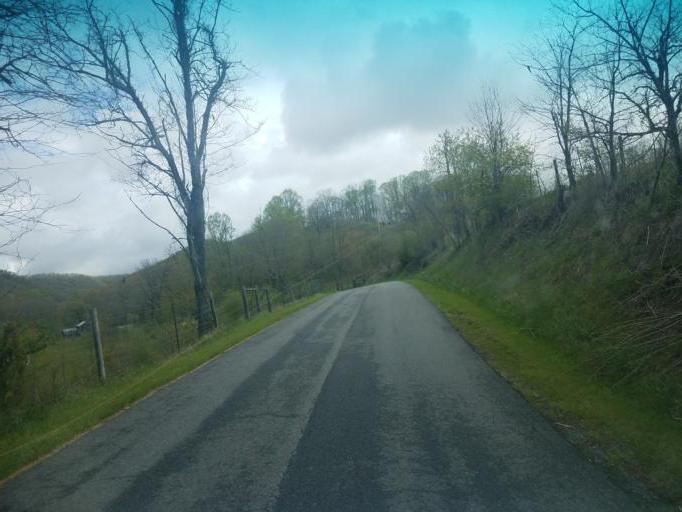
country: US
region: Virginia
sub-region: Smyth County
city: Atkins
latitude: 36.9790
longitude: -81.3954
